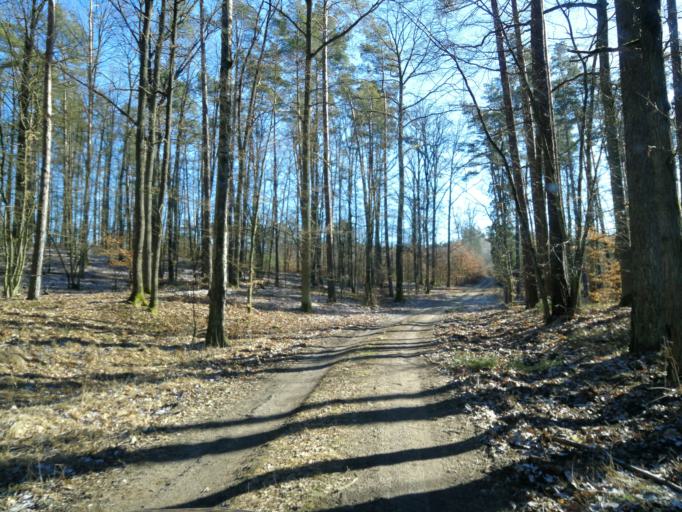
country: PL
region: Kujawsko-Pomorskie
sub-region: Powiat brodnicki
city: Gorzno
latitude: 53.2192
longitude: 19.7095
